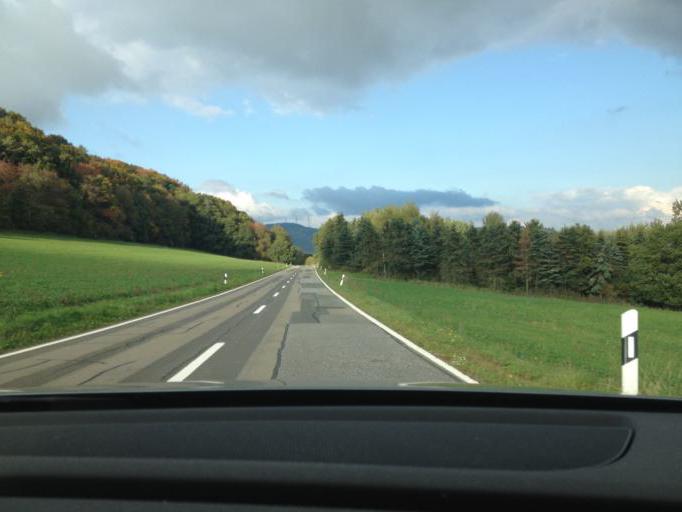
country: DE
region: Saarland
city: Freisen
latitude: 49.5105
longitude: 7.2446
